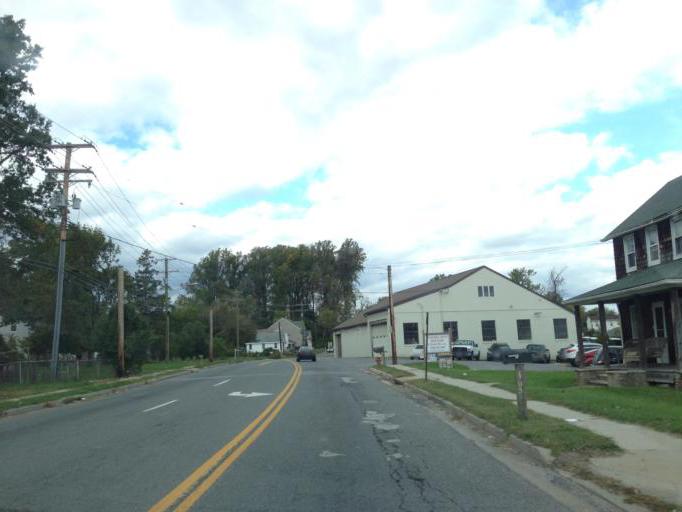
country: US
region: Maryland
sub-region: Baltimore County
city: Milford Mill
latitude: 39.3418
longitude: -76.7629
